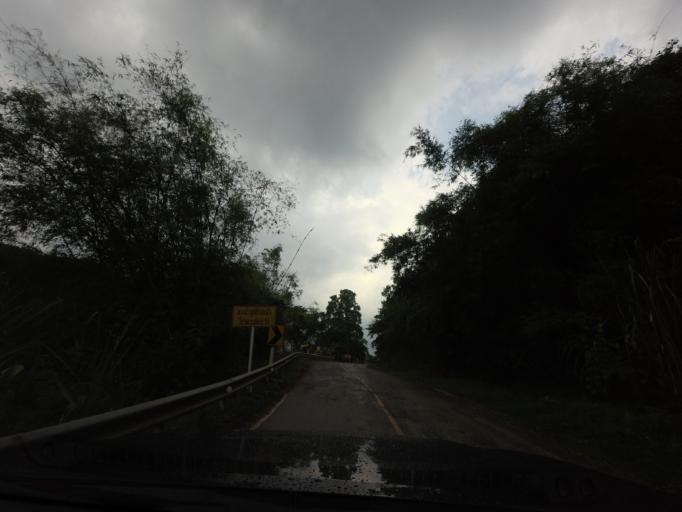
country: TH
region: Nan
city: Bo Kluea
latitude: 19.1677
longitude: 101.1664
